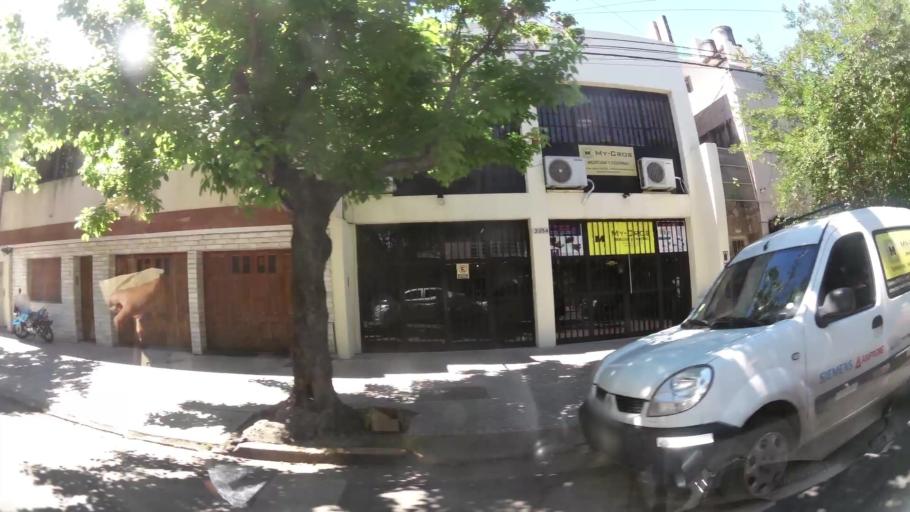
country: AR
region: Santa Fe
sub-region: Departamento de Rosario
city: Rosario
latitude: -32.9351
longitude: -60.6676
